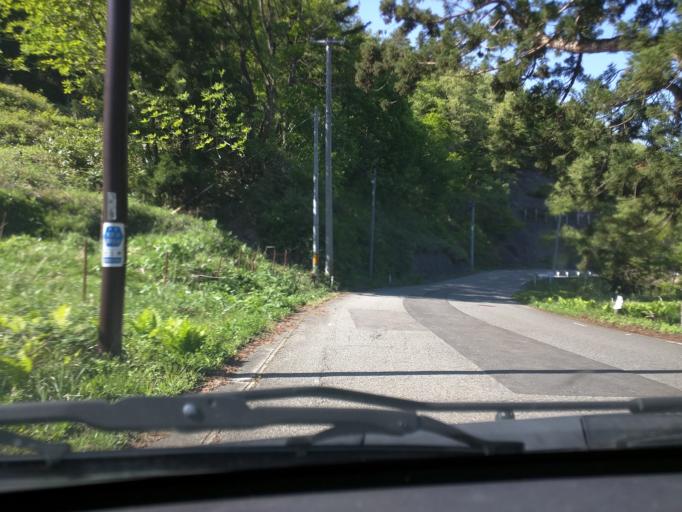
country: JP
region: Fukushima
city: Kitakata
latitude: 37.5607
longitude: 139.6269
